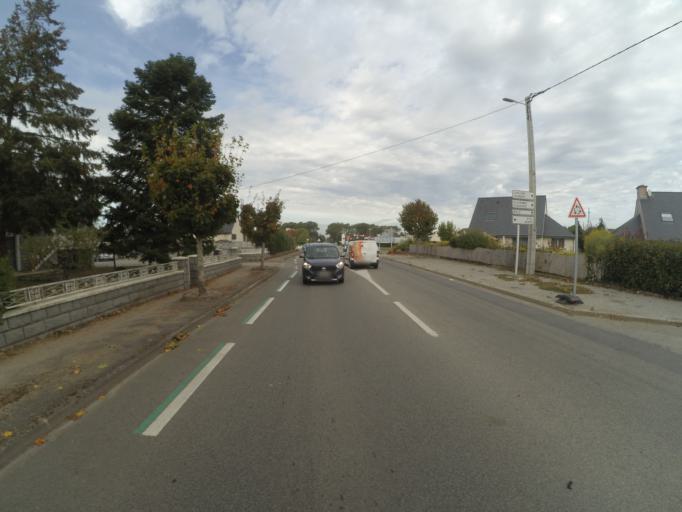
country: FR
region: Brittany
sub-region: Departement du Morbihan
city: Erdeven
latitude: 47.6460
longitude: -3.1590
